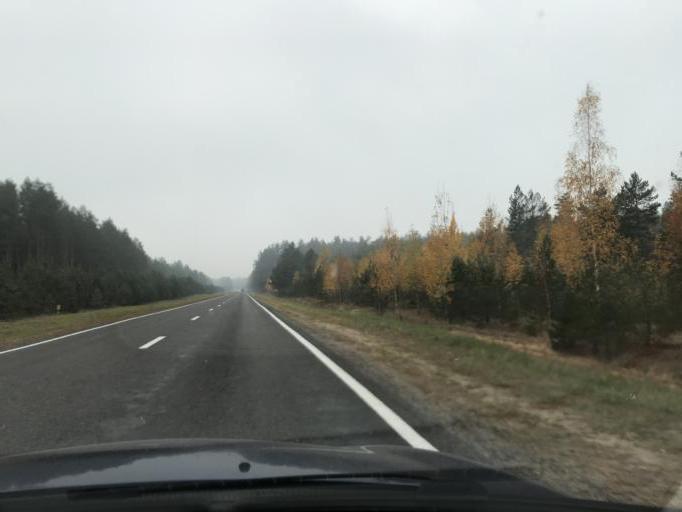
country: LT
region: Alytaus apskritis
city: Druskininkai
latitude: 53.8576
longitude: 23.8923
